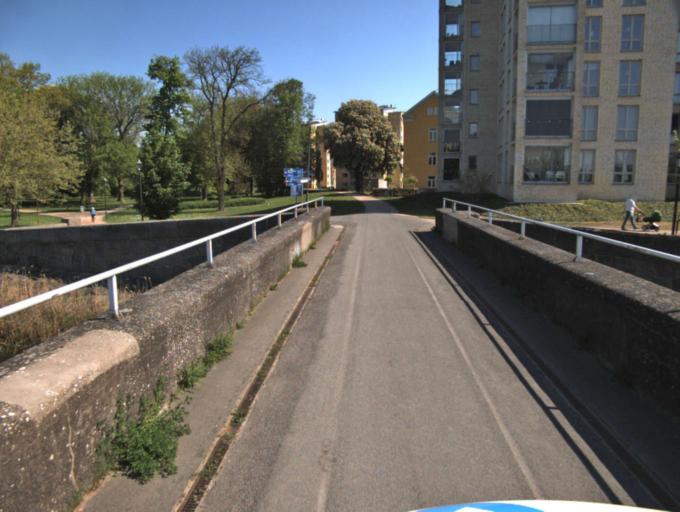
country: SE
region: Skane
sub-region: Kristianstads Kommun
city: Kristianstad
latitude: 56.0250
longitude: 14.1542
